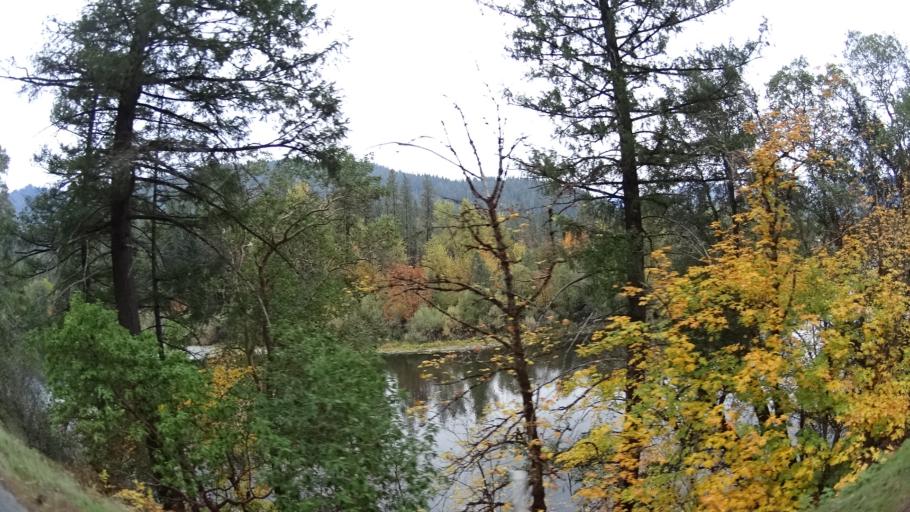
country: US
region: California
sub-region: Siskiyou County
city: Happy Camp
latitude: 41.7871
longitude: -123.3826
